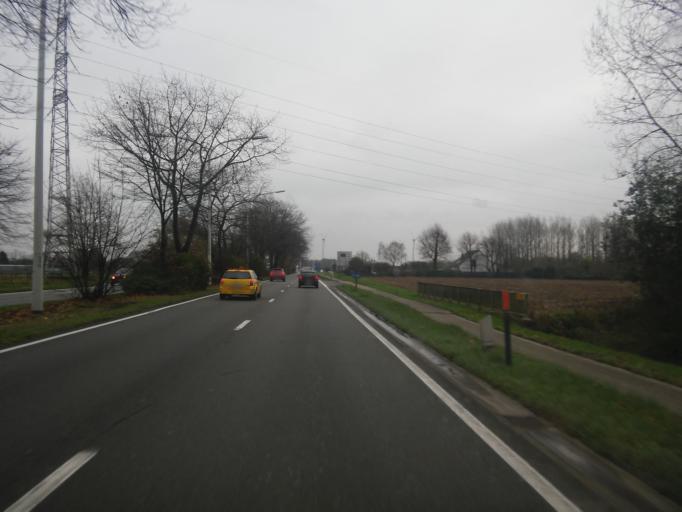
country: BE
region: Flanders
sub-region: Provincie Antwerpen
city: Puurs
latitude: 51.0814
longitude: 4.2906
